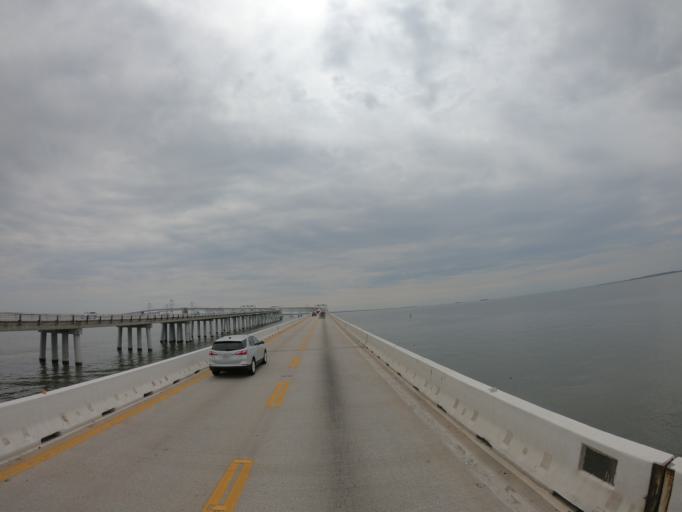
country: US
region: Maryland
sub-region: Anne Arundel County
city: Cape Saint Claire
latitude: 39.0050
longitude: -76.4021
